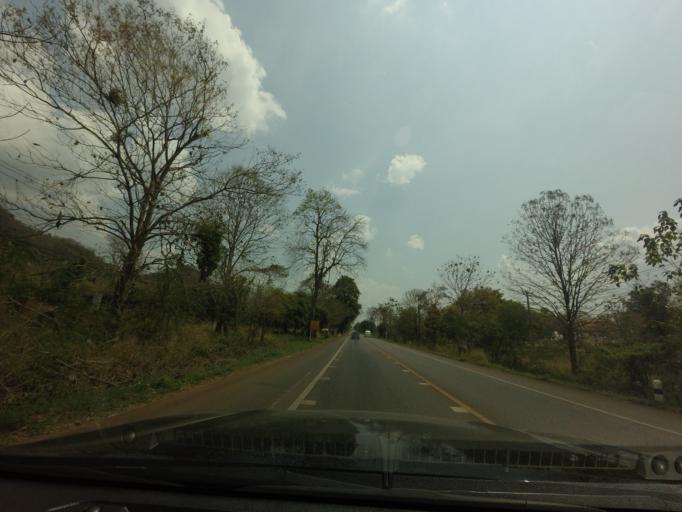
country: TH
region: Kanchanaburi
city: Sai Yok
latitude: 14.1362
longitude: 99.1522
